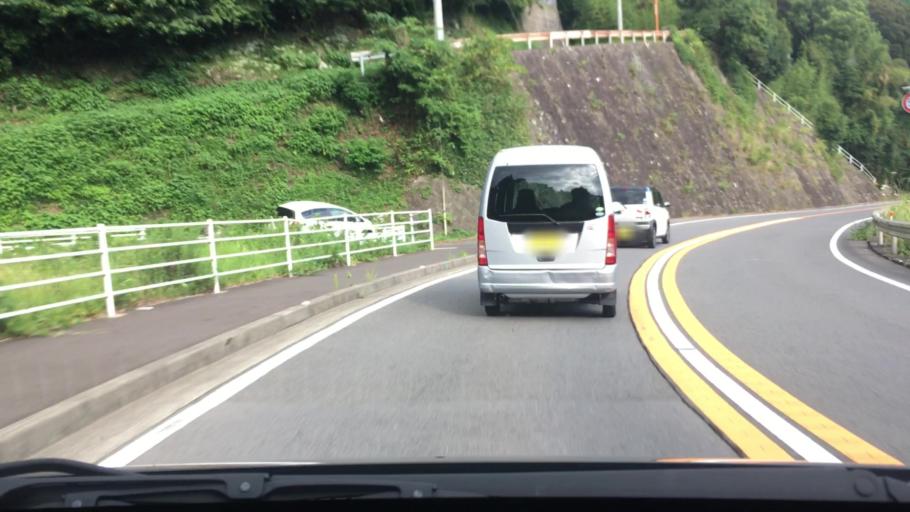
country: JP
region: Nagasaki
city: Togitsu
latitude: 32.8430
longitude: 129.7128
